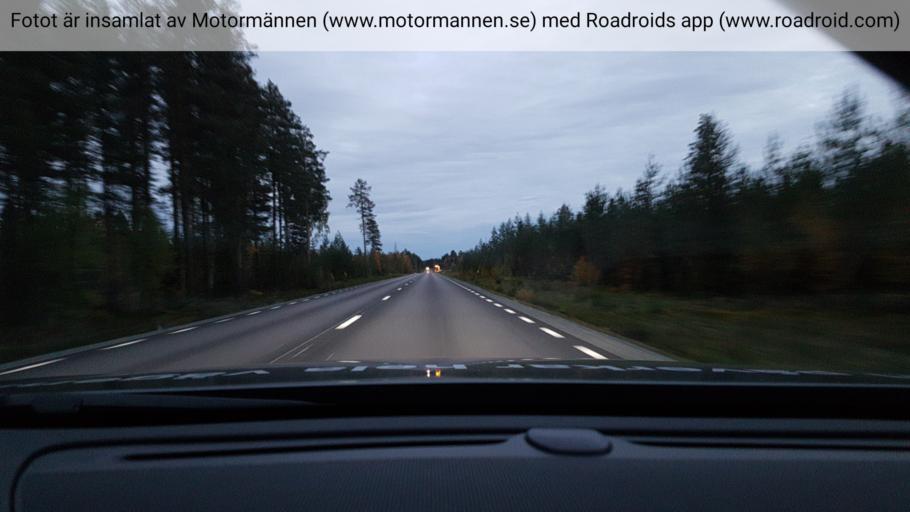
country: SE
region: Norrbotten
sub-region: Alvsbyns Kommun
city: AElvsbyn
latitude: 65.7542
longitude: 20.8973
